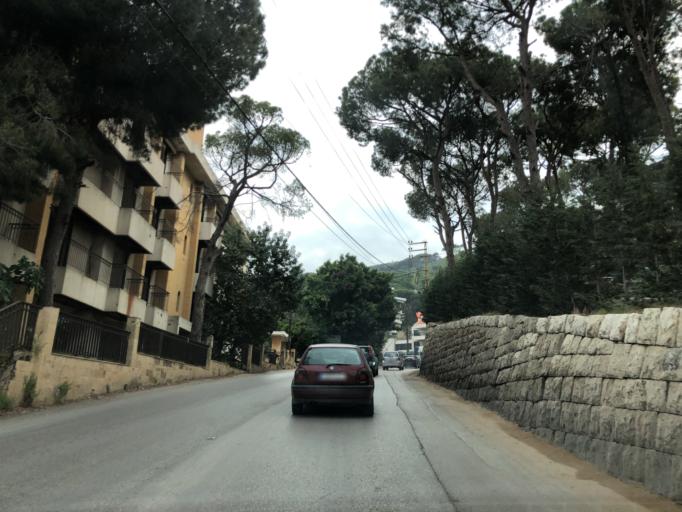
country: LB
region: Mont-Liban
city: Jdaidet el Matn
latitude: 33.8553
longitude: 35.5858
